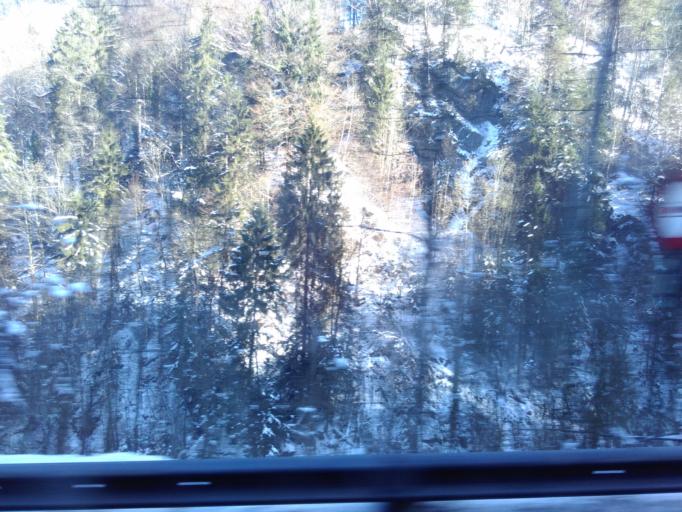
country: CH
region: Schwyz
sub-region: Bezirk March
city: Schubelbach
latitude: 47.1606
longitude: 8.8926
